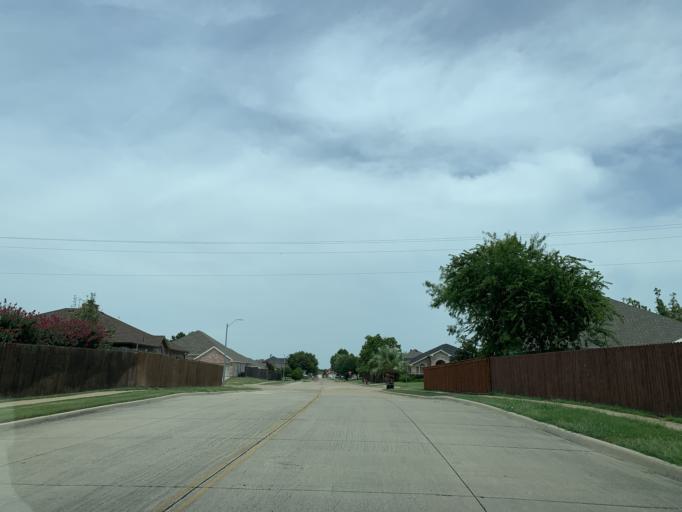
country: US
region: Texas
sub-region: Dallas County
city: Grand Prairie
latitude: 32.6605
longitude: -97.0209
